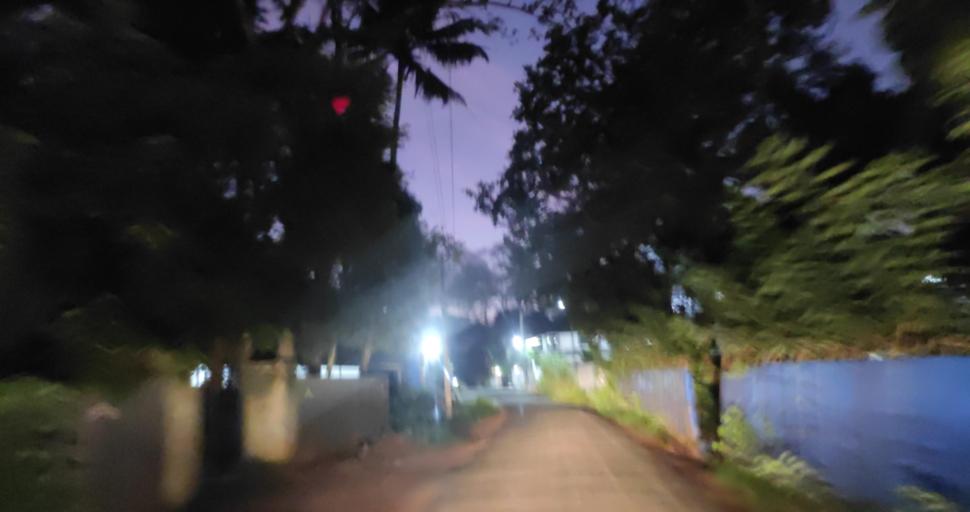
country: IN
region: Kerala
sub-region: Alappuzha
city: Shertallai
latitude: 9.6241
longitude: 76.3471
